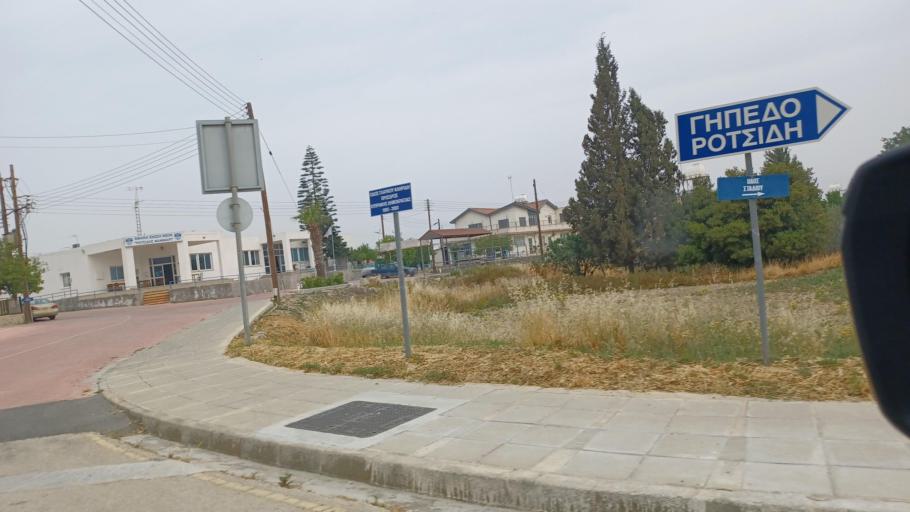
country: CY
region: Lefkosia
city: Mammari
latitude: 35.1754
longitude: 33.2051
